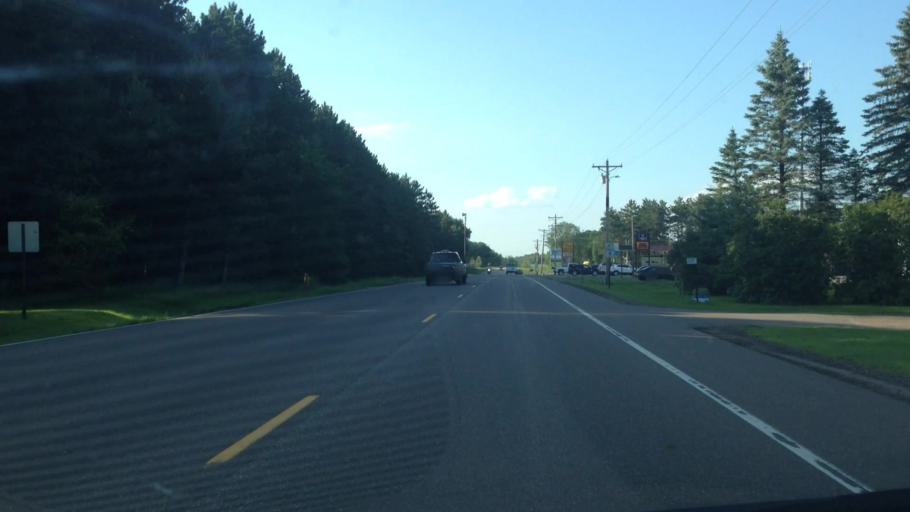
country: US
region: Minnesota
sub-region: Sherburne County
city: Big Lake
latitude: 45.4447
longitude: -93.7360
